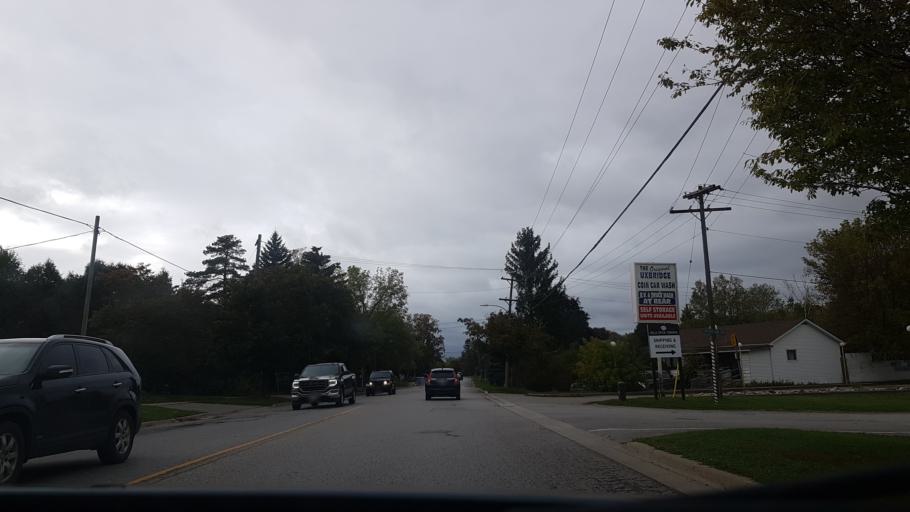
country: CA
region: Ontario
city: Uxbridge
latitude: 44.1048
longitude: -79.1128
